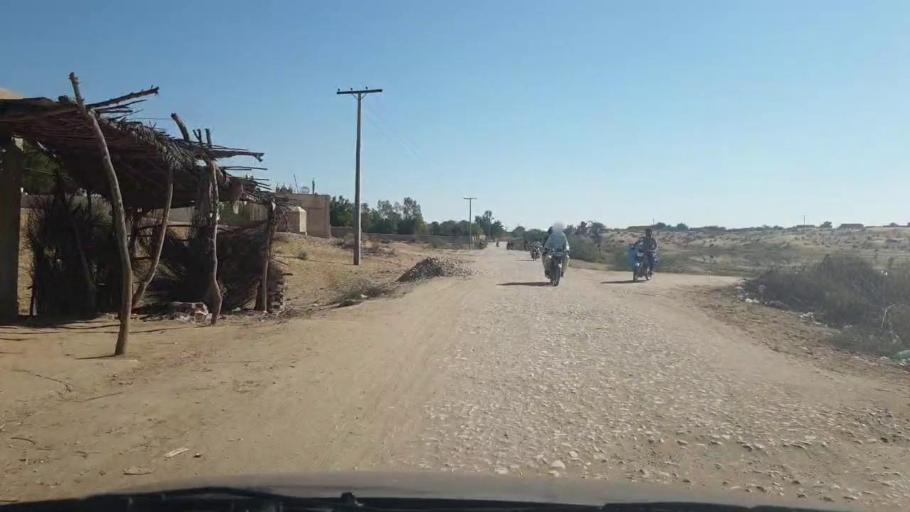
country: PK
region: Sindh
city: Bozdar
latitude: 27.0635
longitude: 68.6238
